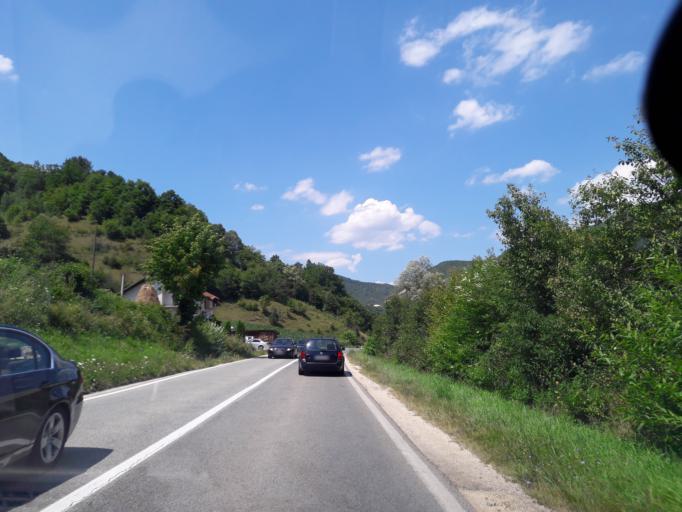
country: BA
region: Republika Srpska
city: Mrkonjic Grad
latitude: 44.3572
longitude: 17.1623
